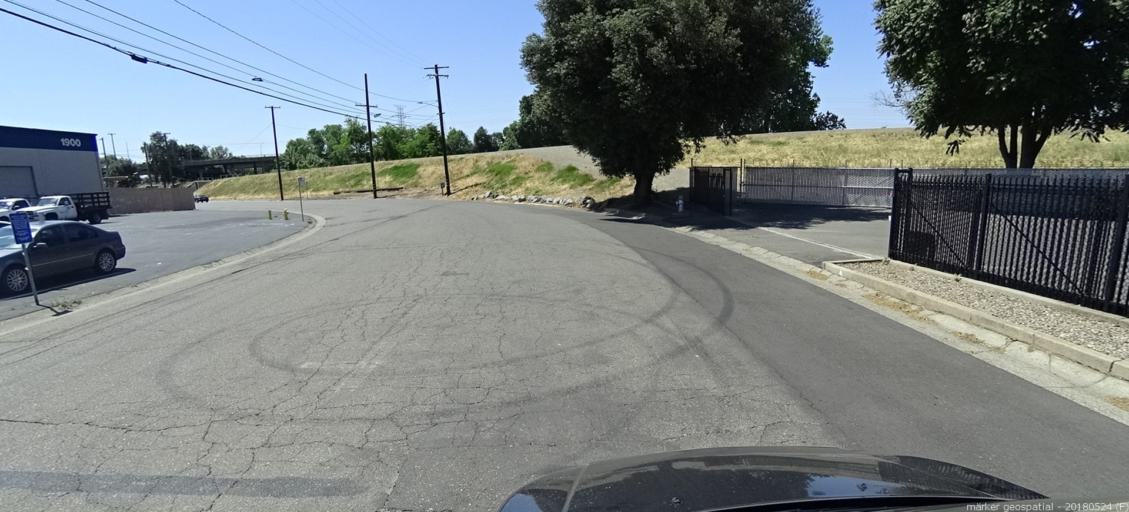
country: US
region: California
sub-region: Sacramento County
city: Sacramento
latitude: 38.6016
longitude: -121.4714
